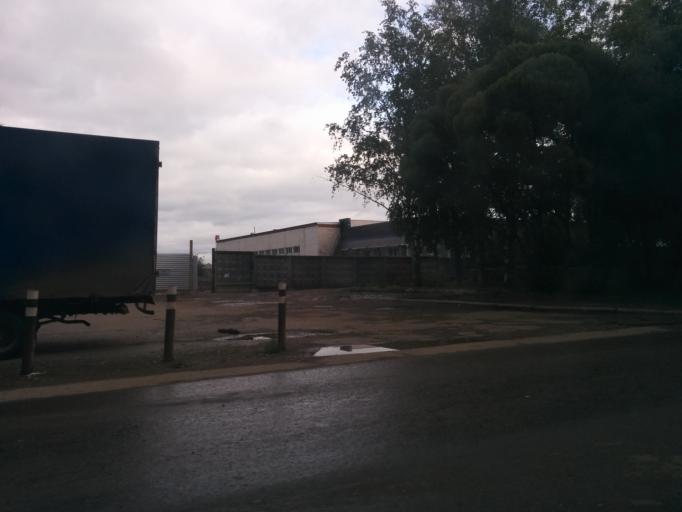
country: RU
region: Perm
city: Perm
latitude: 57.9984
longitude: 56.3020
